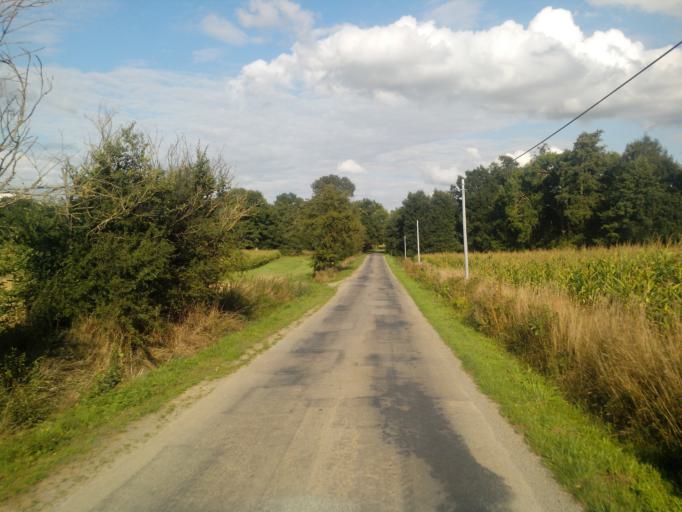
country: FR
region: Brittany
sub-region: Departement d'Ille-et-Vilaine
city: Iffendic
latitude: 48.1124
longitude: -2.0783
